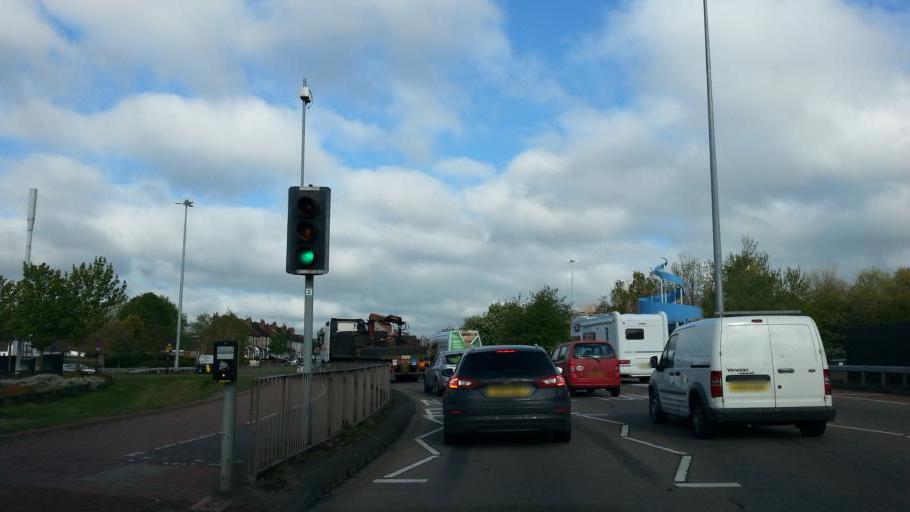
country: GB
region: England
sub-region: Warwickshire
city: Exhall
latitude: 52.4352
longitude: -1.4931
